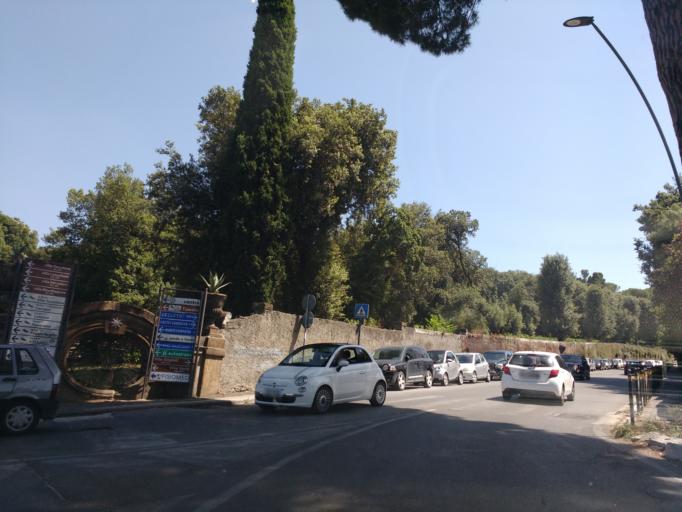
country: IT
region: Latium
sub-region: Citta metropolitana di Roma Capitale
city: Armetta
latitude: 41.8053
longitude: 12.6803
